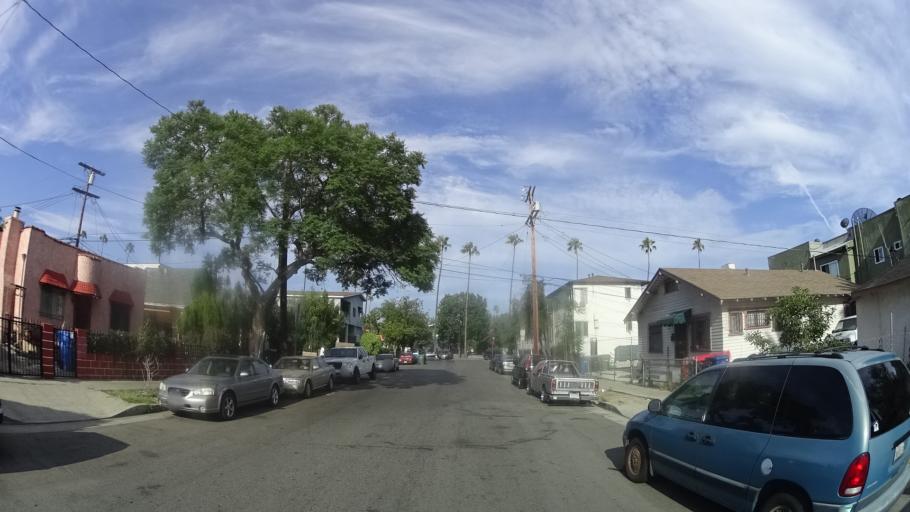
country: US
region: California
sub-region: Los Angeles County
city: Hollywood
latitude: 34.0862
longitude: -118.3014
